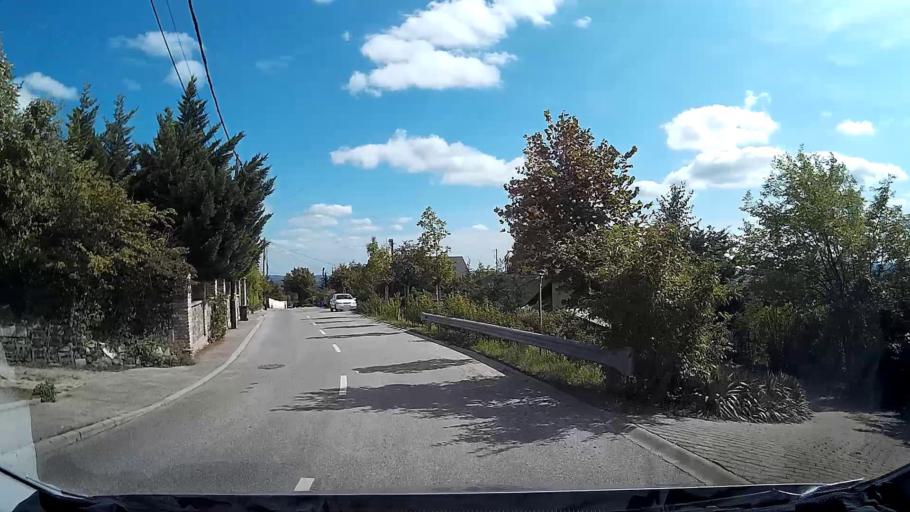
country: HU
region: Pest
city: Szentendre
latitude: 47.6945
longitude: 19.0614
